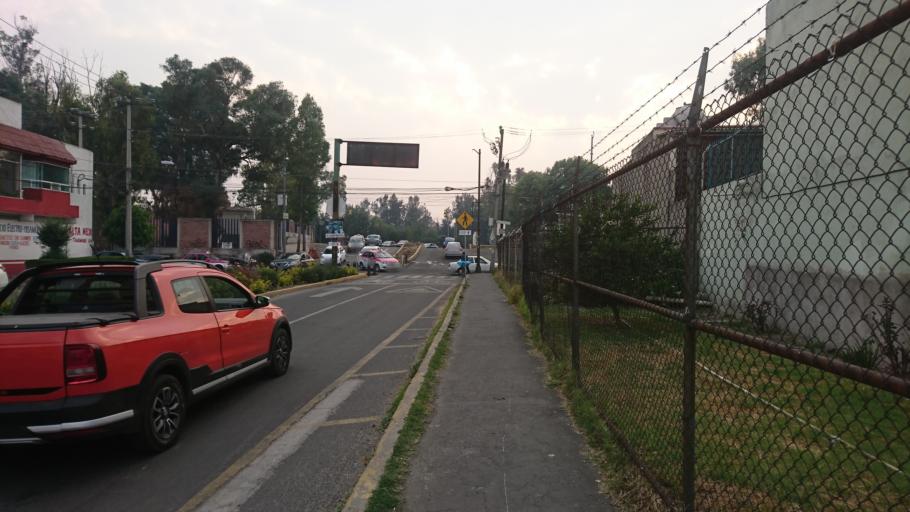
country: MX
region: Mexico City
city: Iztapalapa
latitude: 19.3205
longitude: -99.0983
